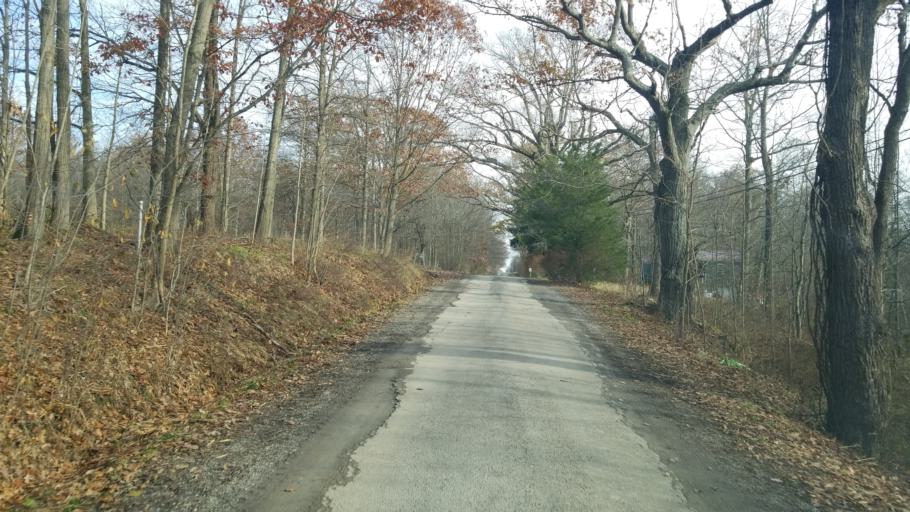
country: US
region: Ohio
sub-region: Ashtabula County
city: Roaming Shores
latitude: 41.6433
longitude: -80.7744
